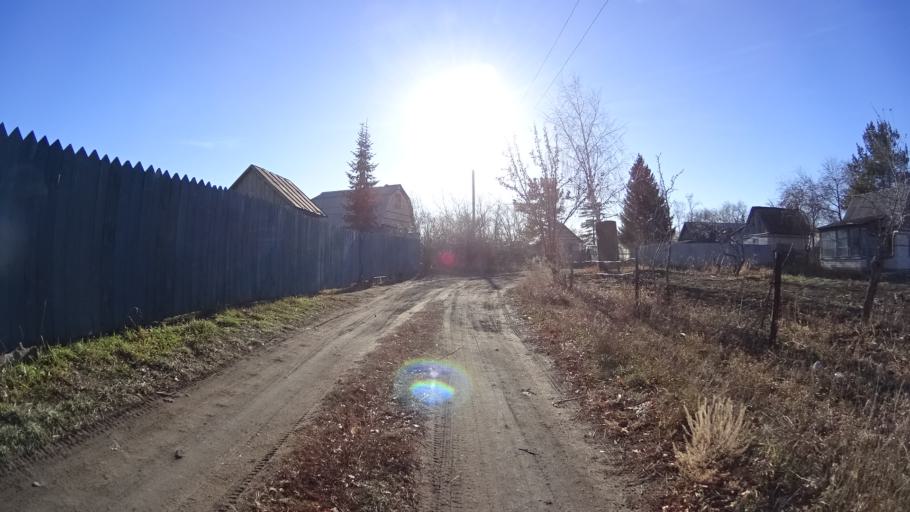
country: RU
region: Chelyabinsk
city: Troitsk
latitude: 54.0821
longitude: 61.5101
